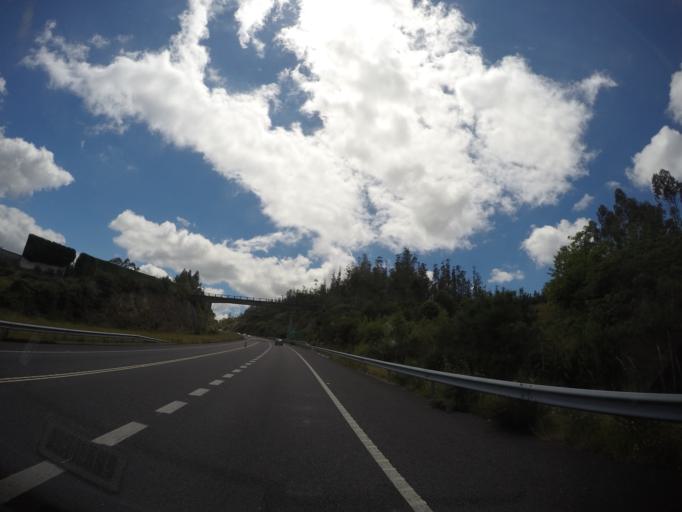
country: ES
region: Aragon
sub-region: Provincia de Zaragoza
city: El Burgo de Ebro
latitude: 41.5553
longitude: -0.7613
